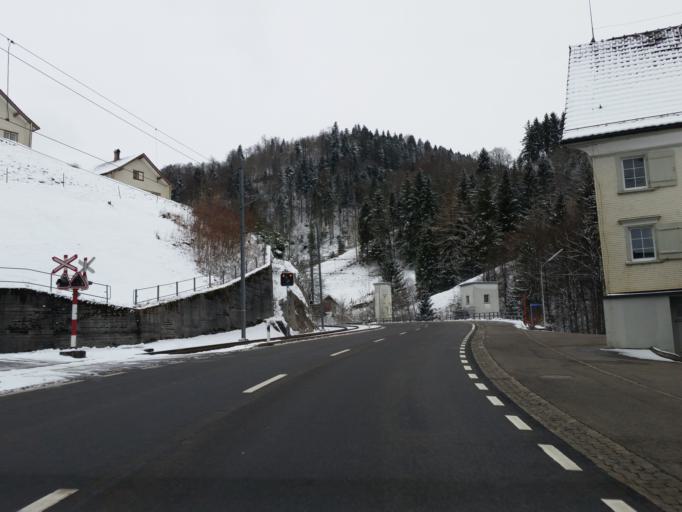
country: CH
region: Appenzell Ausserrhoden
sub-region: Bezirk Mittelland
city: Buhler
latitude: 47.3681
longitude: 9.4314
